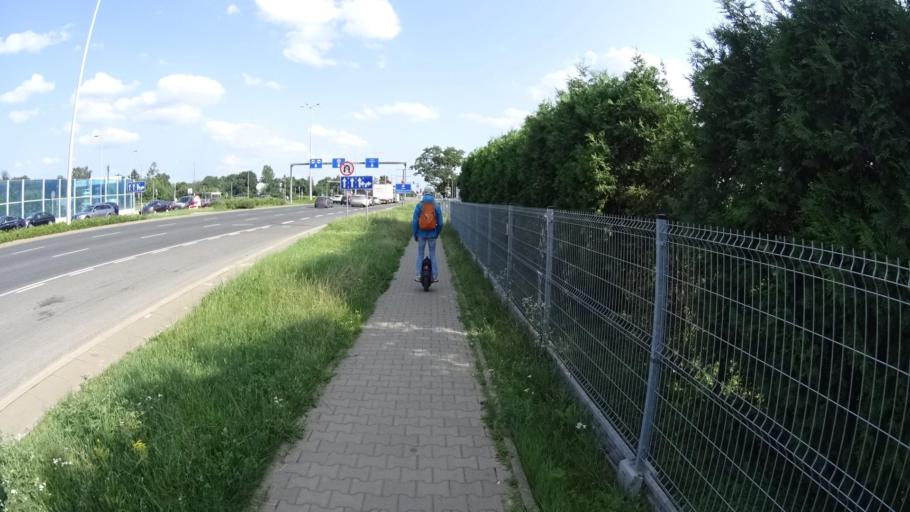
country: PL
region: Masovian Voivodeship
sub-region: Warszawa
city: Bialoleka
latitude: 52.3514
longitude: 20.9475
